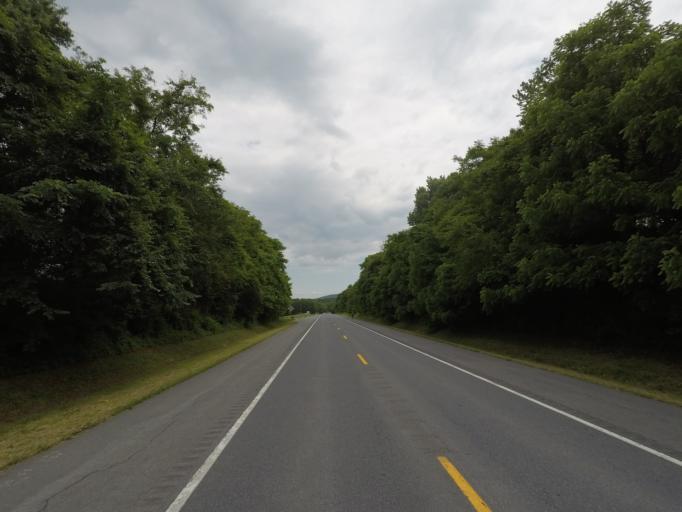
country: US
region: Maryland
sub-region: Frederick County
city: Brunswick
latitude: 39.3719
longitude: -77.6691
